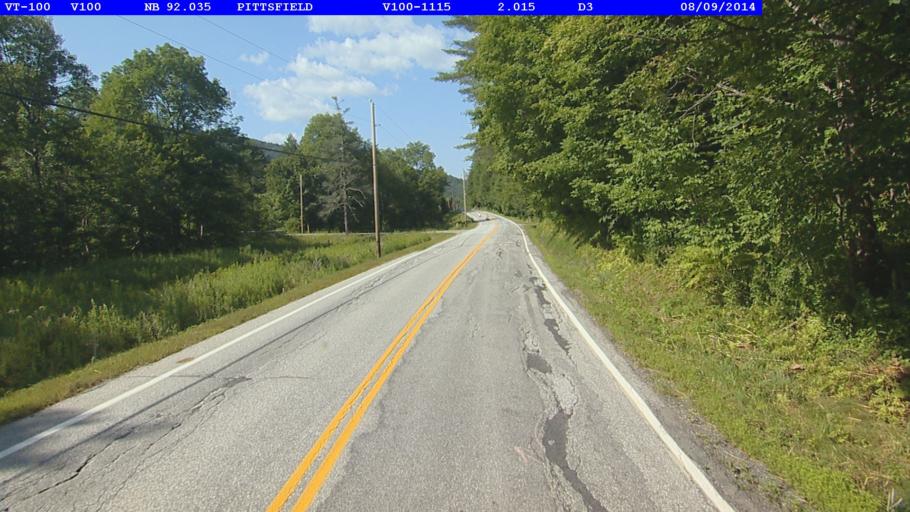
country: US
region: Vermont
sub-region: Rutland County
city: Rutland
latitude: 43.7459
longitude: -72.8205
